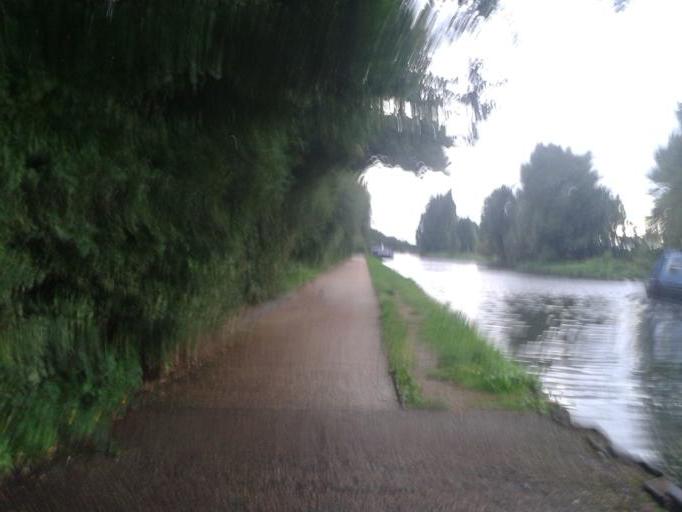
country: GB
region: England
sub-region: Greater London
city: Walthamstow
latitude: 51.6049
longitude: -0.0423
